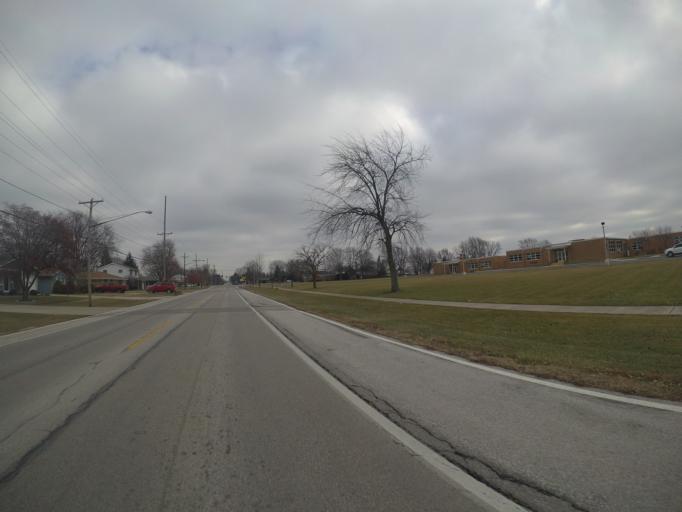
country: US
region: Ohio
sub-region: Lucas County
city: Oregon
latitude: 41.6443
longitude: -83.4704
